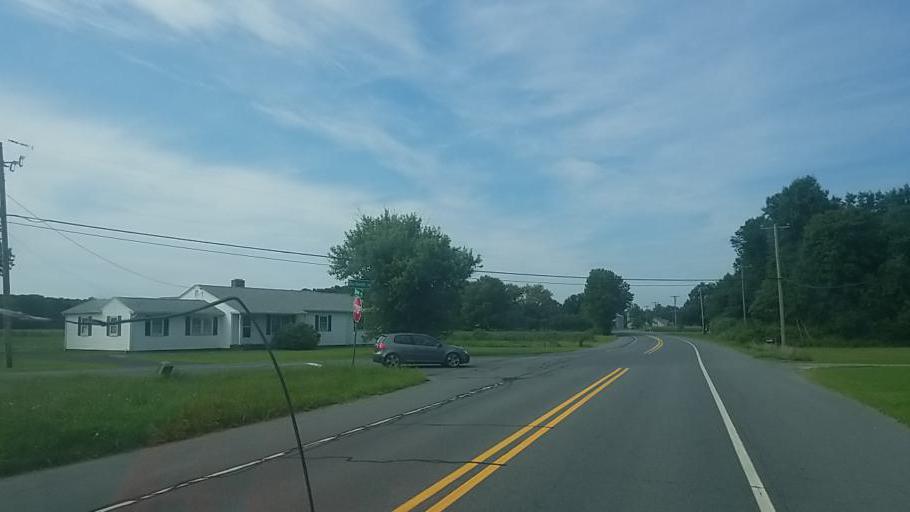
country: US
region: Delaware
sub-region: Sussex County
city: Selbyville
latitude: 38.5330
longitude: -75.1903
